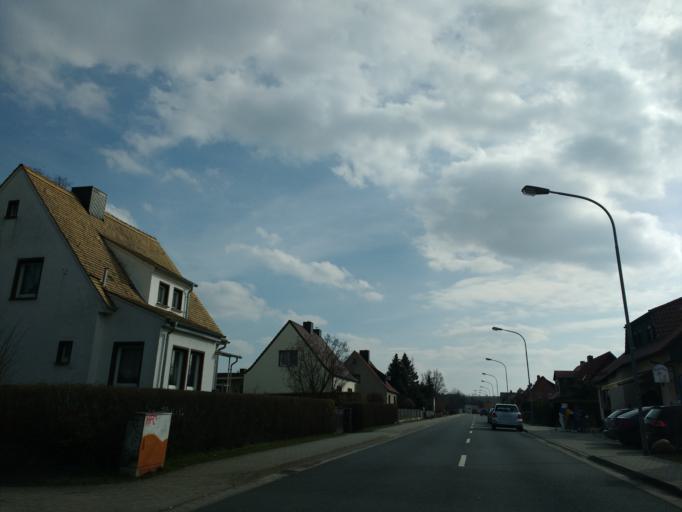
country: DE
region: Saxony-Anhalt
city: Roblingen am See
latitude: 51.4557
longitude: 11.6710
